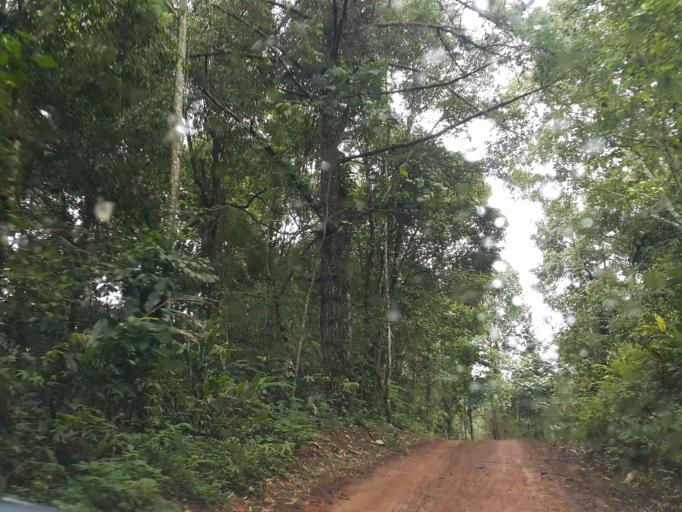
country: TH
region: Chiang Mai
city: Mae Chaem
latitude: 18.5050
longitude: 98.5281
